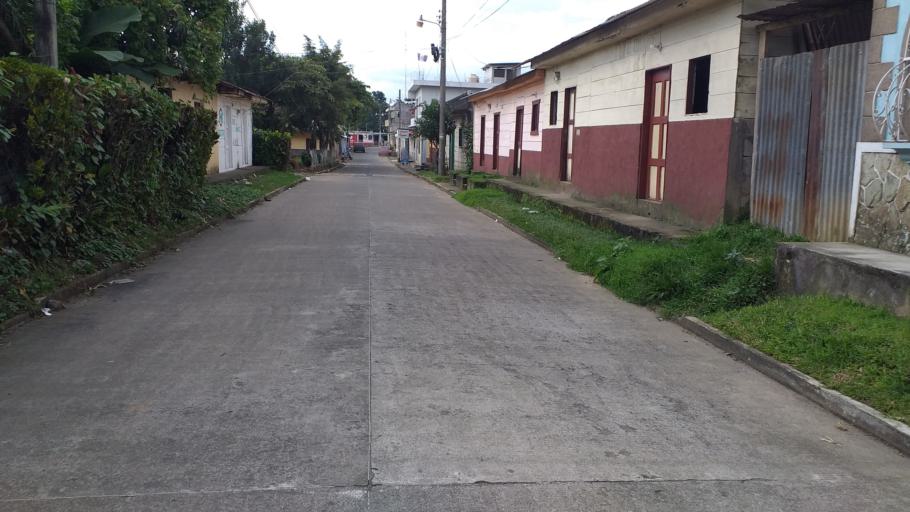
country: GT
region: Suchitepeque
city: Pueblo Nuevo
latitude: 14.6453
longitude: -91.5568
